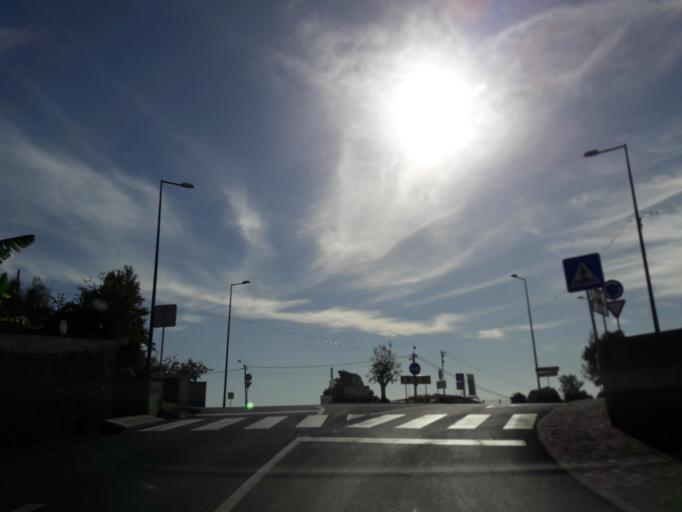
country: PT
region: Madeira
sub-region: Funchal
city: Nossa Senhora do Monte
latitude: 32.6708
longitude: -16.9218
